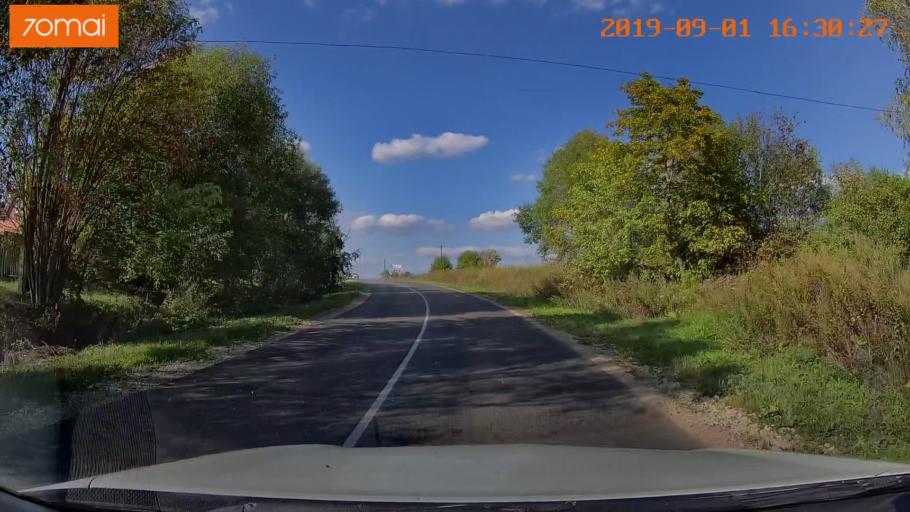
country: RU
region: Kaluga
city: Maloyaroslavets
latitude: 54.9452
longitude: 36.4587
